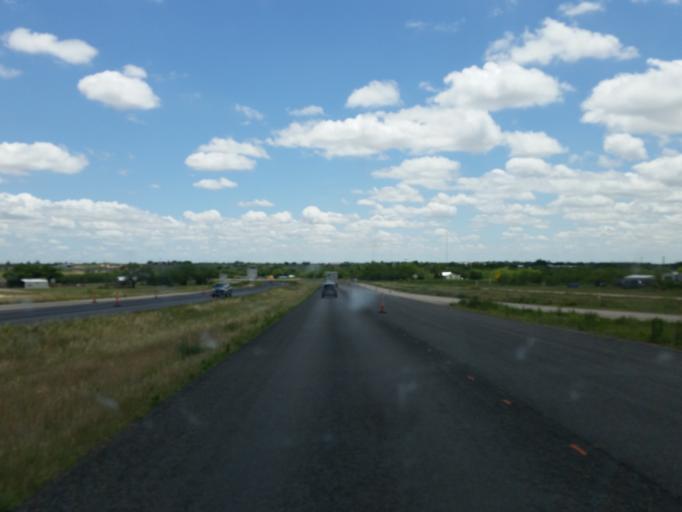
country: US
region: Texas
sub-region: Scurry County
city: Snyder
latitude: 32.7374
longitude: -100.9161
